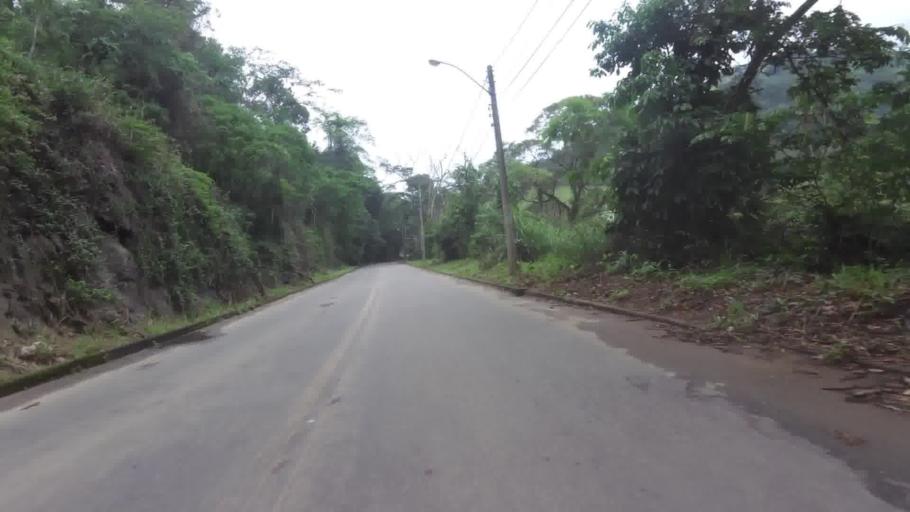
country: BR
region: Espirito Santo
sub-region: Iconha
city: Iconha
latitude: -20.7762
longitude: -40.8273
